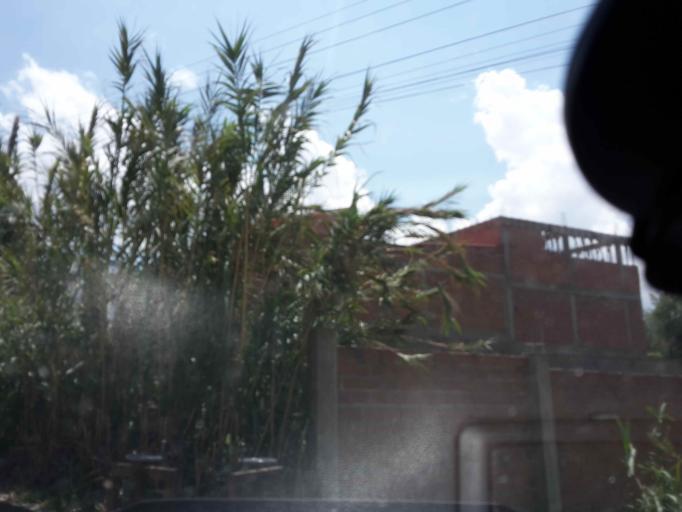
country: BO
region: Cochabamba
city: Cochabamba
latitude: -17.3509
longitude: -66.2138
